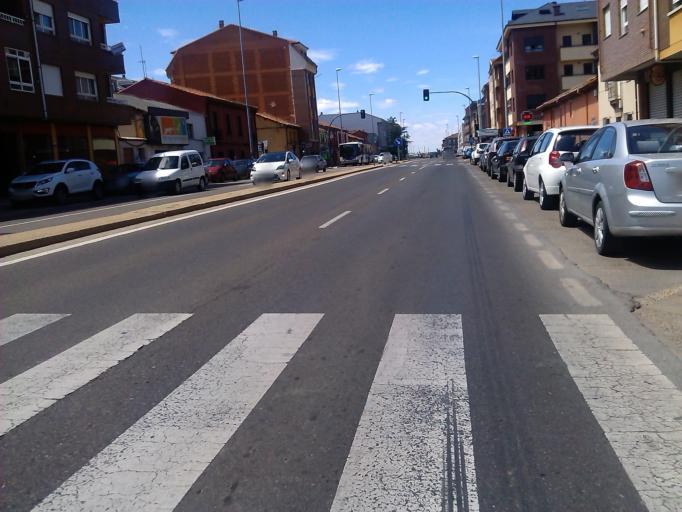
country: ES
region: Castille and Leon
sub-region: Provincia de Leon
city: San Andres del Rabanedo
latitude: 42.5816
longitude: -5.6386
